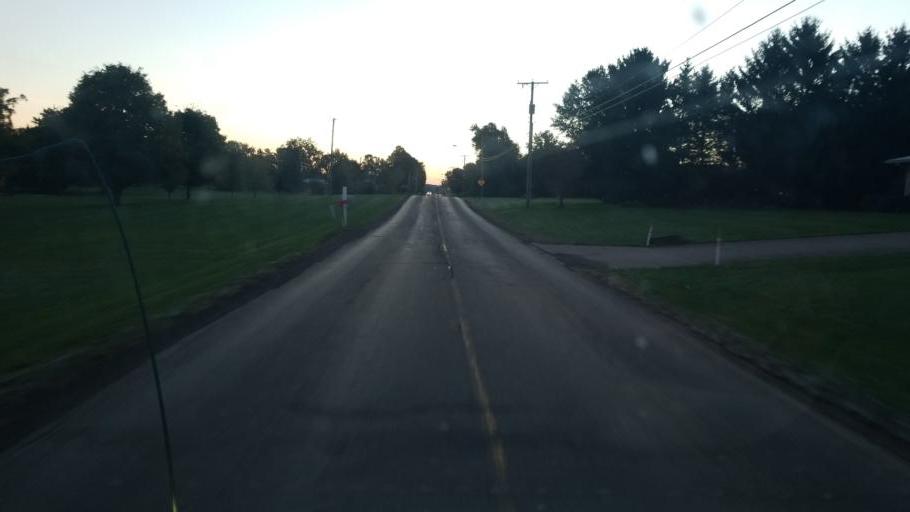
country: US
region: Ohio
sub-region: Wayne County
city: Apple Creek
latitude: 40.7412
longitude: -81.7593
